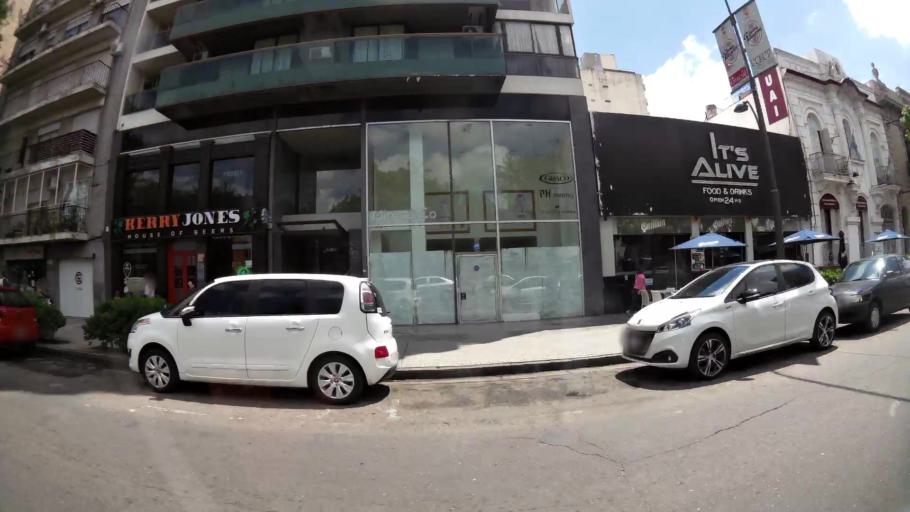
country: AR
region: Santa Fe
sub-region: Departamento de Rosario
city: Rosario
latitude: -32.9554
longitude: -60.6511
